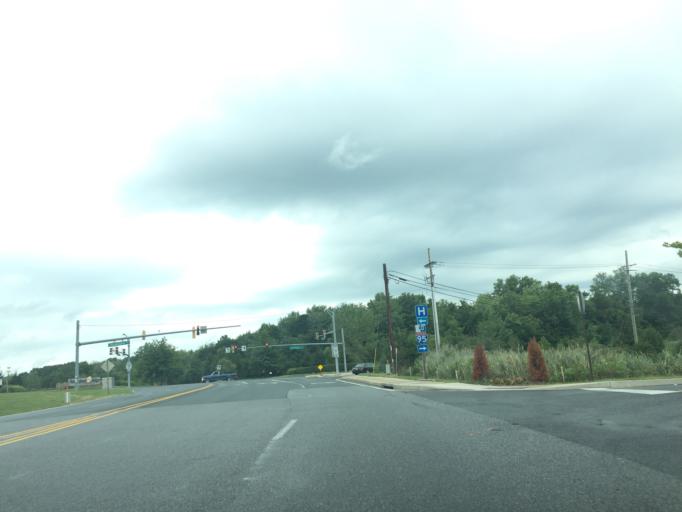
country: US
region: Maryland
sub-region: Baltimore County
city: White Marsh
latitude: 39.3745
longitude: -76.4402
